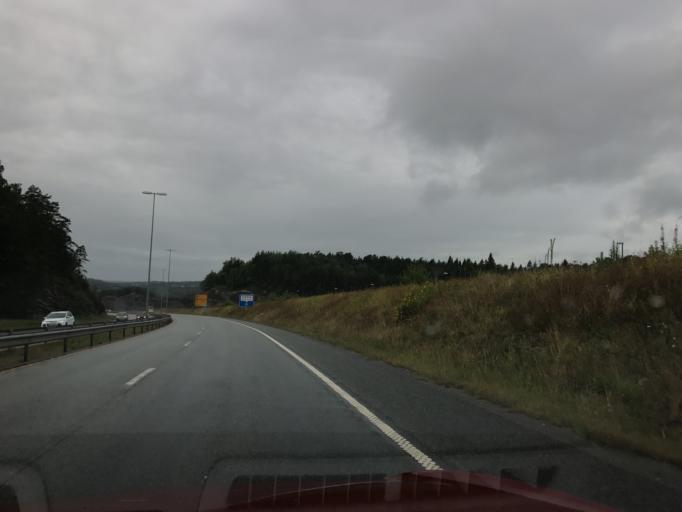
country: NO
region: Vest-Agder
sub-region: Kristiansand
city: Tveit
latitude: 58.1795
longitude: 8.1149
